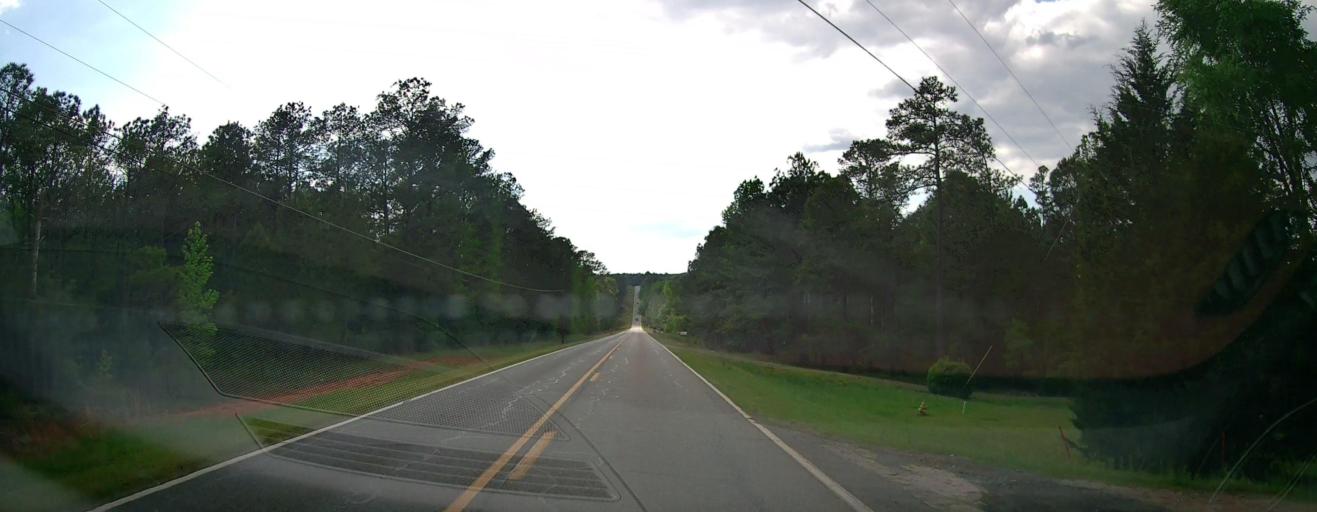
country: US
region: Georgia
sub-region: Baldwin County
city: Hardwick
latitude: 33.0623
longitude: -83.1537
